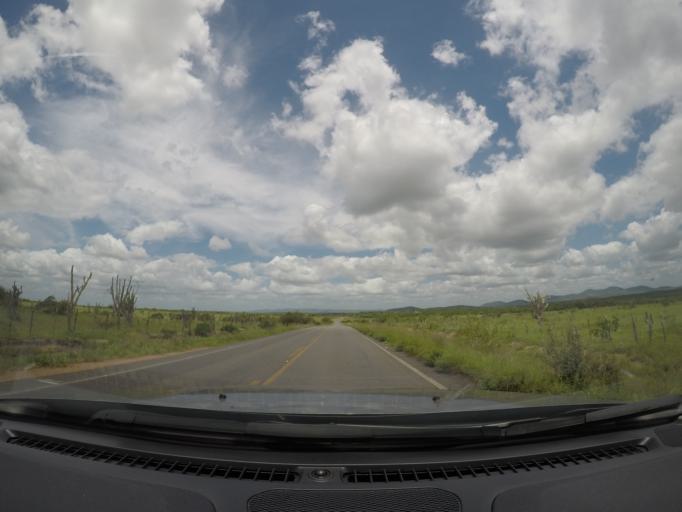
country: BR
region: Bahia
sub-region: Ipira
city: Ipira
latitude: -12.2941
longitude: -39.8836
